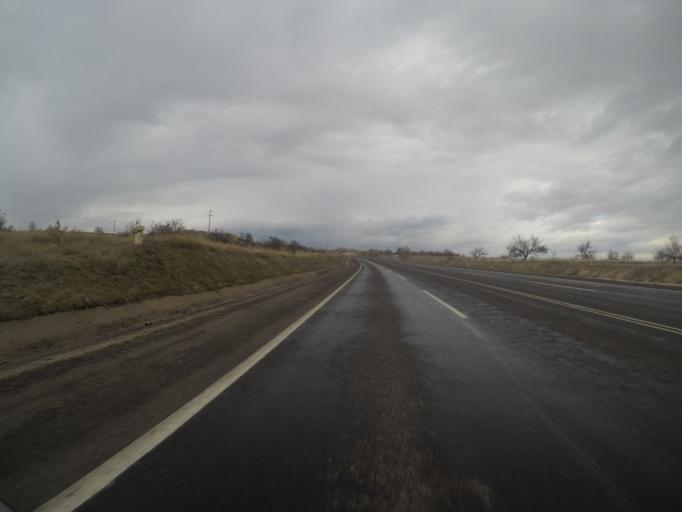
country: TR
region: Nevsehir
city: Urgub
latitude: 38.6352
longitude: 34.8745
